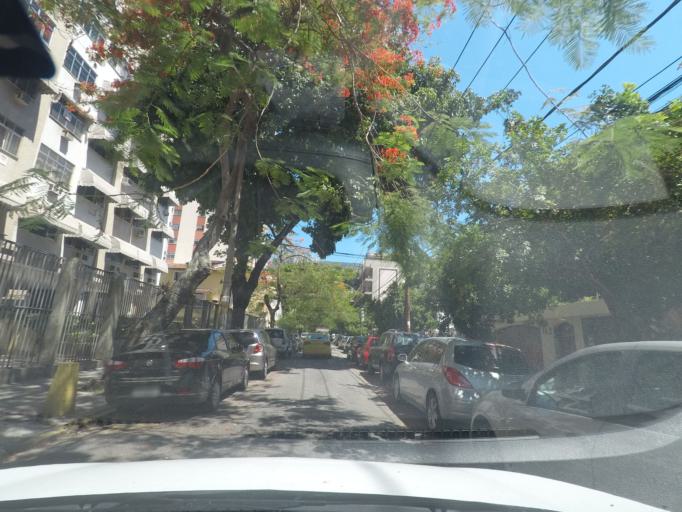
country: BR
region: Rio de Janeiro
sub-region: Rio De Janeiro
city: Rio de Janeiro
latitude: -22.9200
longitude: -43.2366
